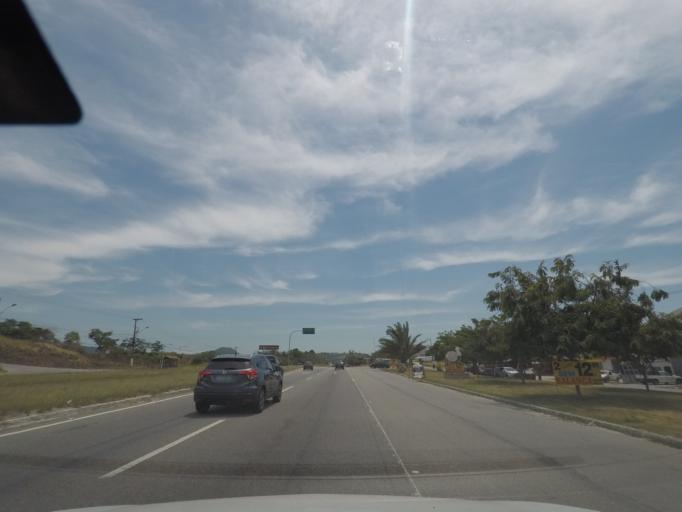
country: BR
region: Rio de Janeiro
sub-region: Marica
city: Marica
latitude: -22.9150
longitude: -42.8476
